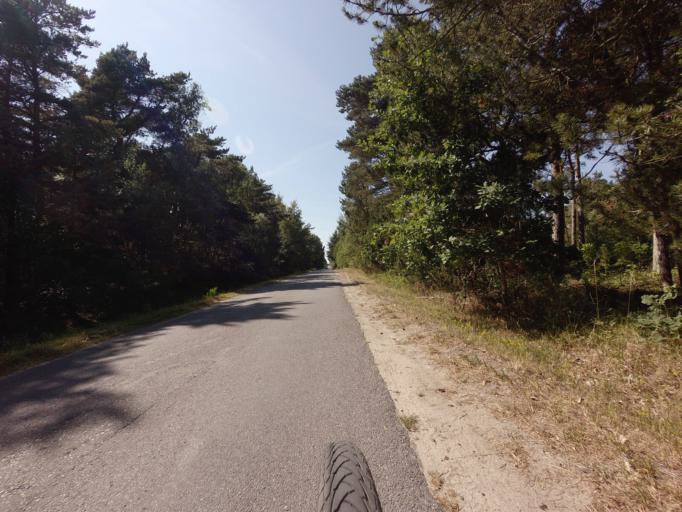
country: DK
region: North Denmark
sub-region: Laeso Kommune
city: Byrum
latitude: 57.2940
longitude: 10.9407
